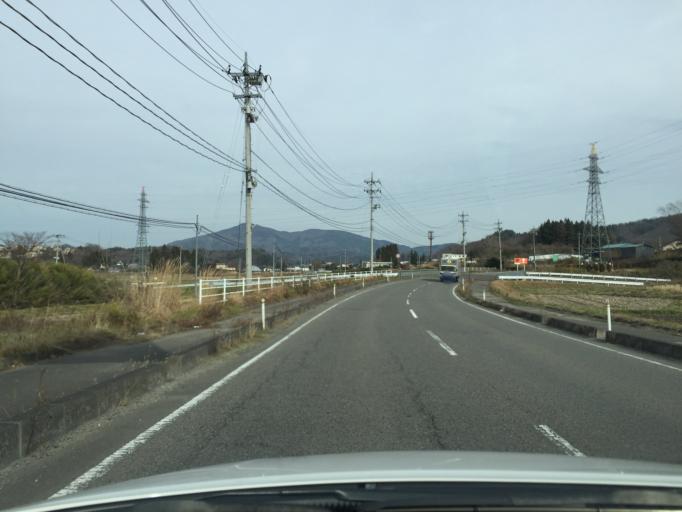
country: JP
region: Fukushima
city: Funehikimachi-funehiki
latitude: 37.4272
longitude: 140.5874
